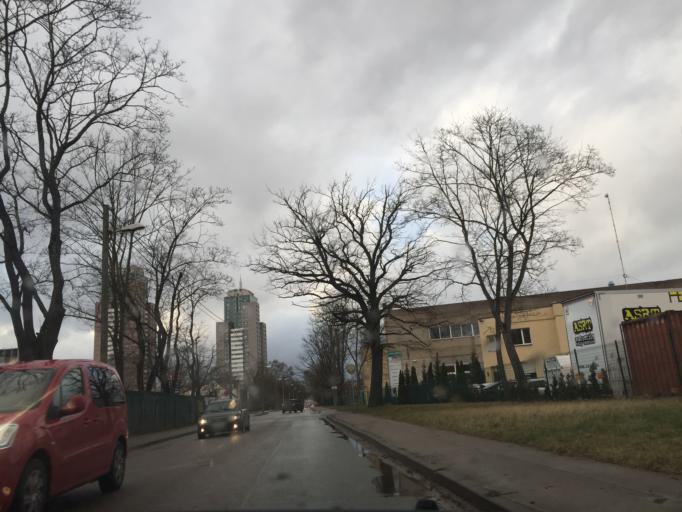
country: LV
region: Marupe
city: Marupe
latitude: 56.9320
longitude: 24.0496
